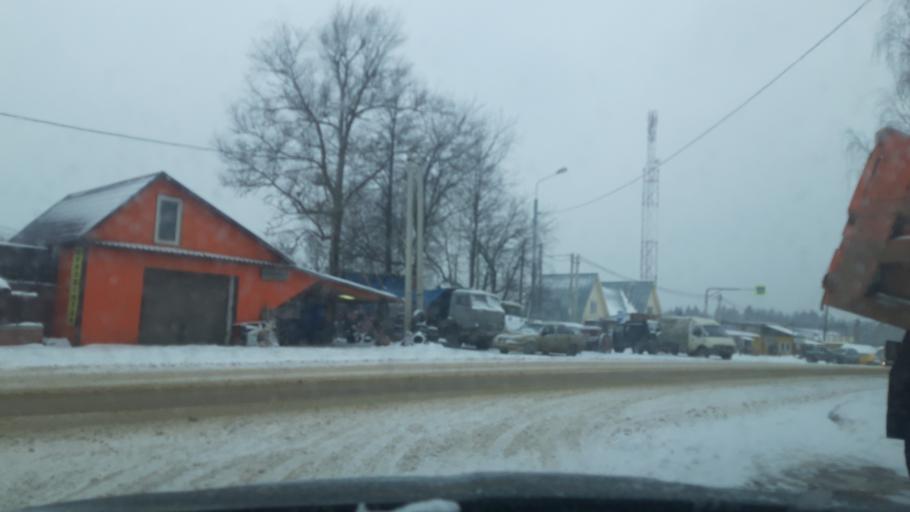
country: RU
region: Moskovskaya
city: Avtopoligon
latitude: 56.2569
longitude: 37.2279
